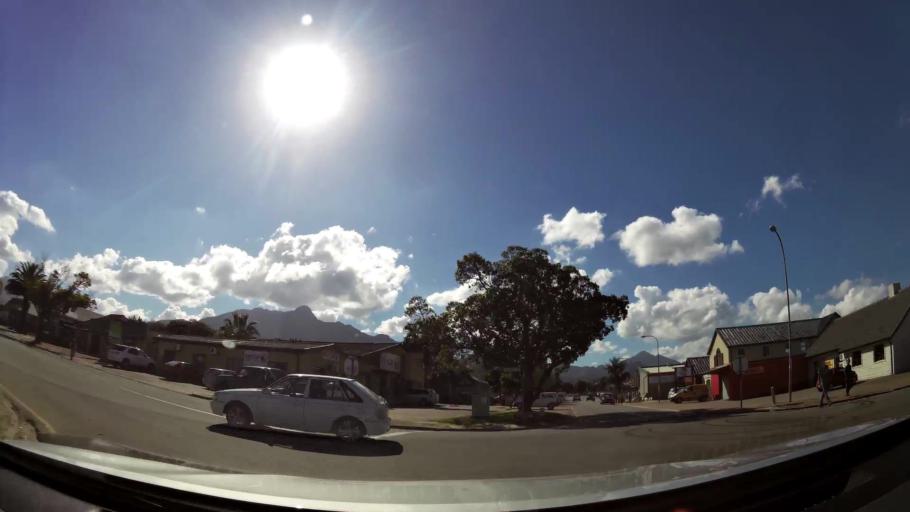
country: ZA
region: Western Cape
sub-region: Eden District Municipality
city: George
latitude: -33.9651
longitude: 22.4642
